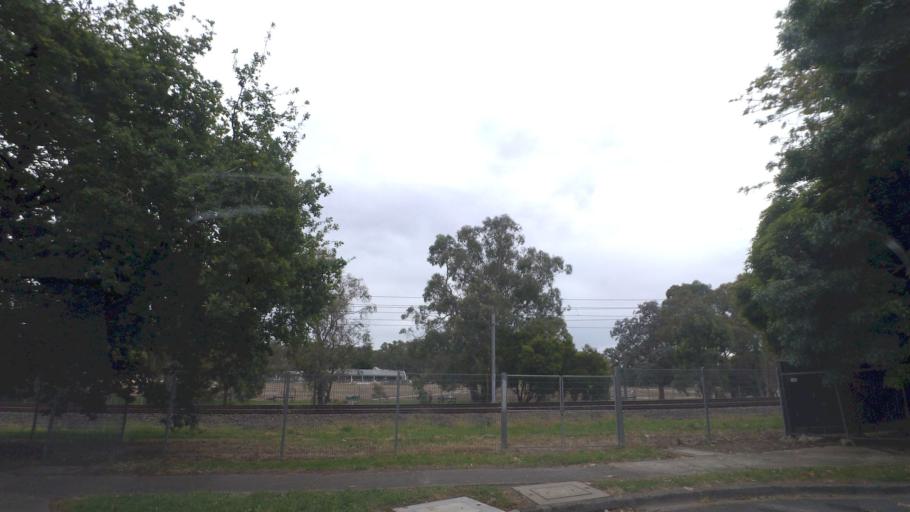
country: AU
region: Victoria
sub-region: Maroondah
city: Croydon North
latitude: -37.7891
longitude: 145.2893
